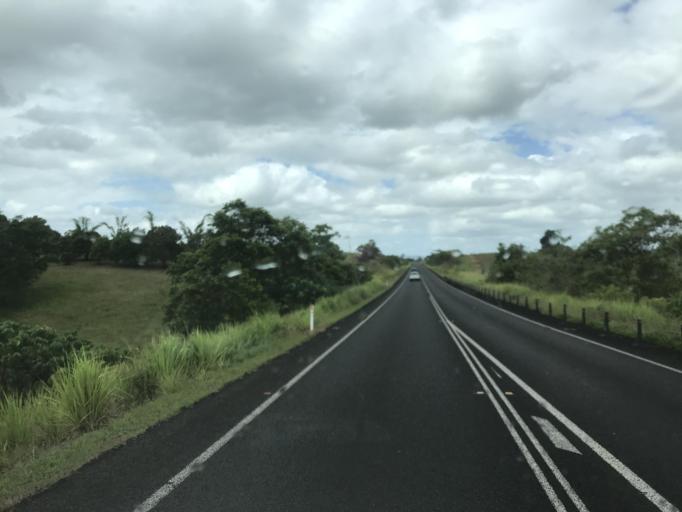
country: AU
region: Queensland
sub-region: Cassowary Coast
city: Innisfail
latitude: -17.5788
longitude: 145.9840
